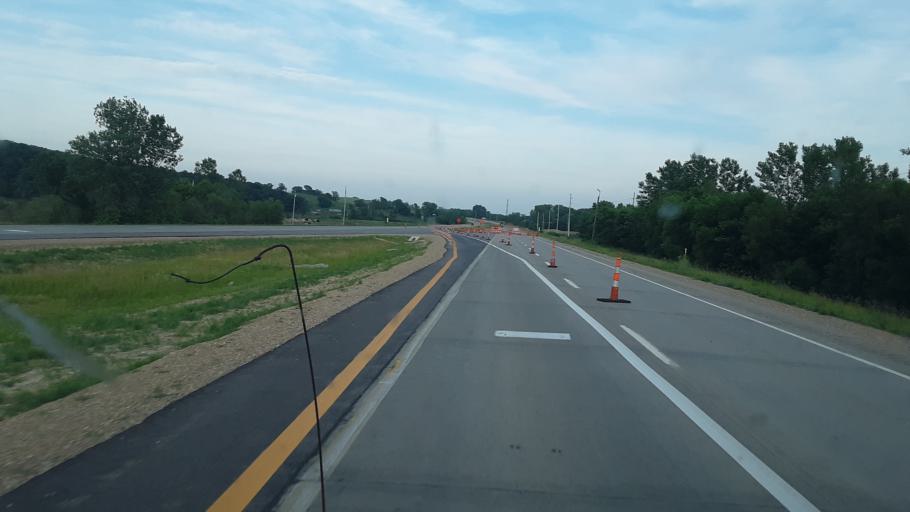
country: US
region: Iowa
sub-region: Tama County
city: Toledo
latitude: 42.0019
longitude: -92.7125
